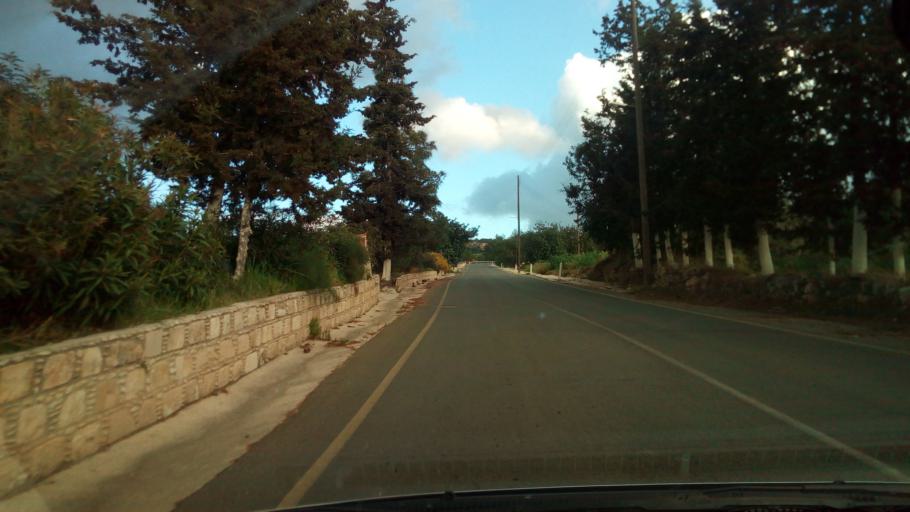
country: CY
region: Pafos
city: Polis
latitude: 34.9893
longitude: 32.4922
